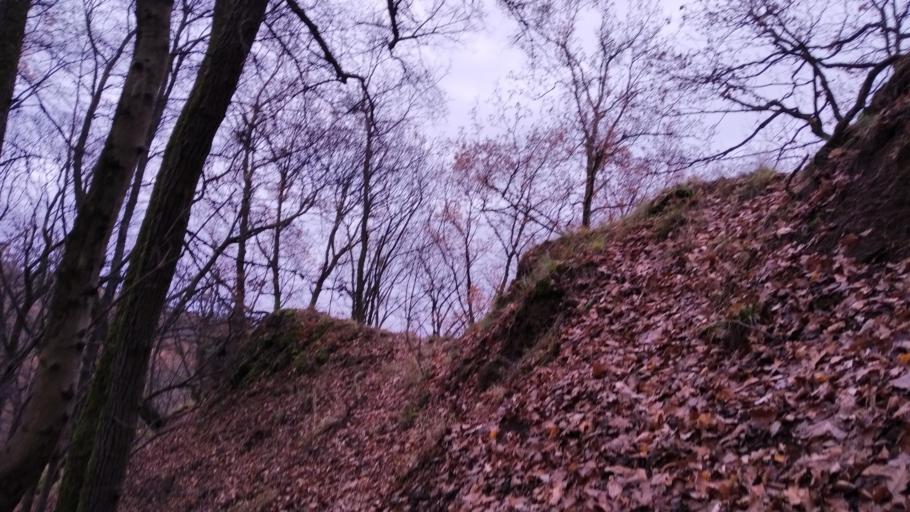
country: HU
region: Pest
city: Csobanka
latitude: 47.6812
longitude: 18.9547
